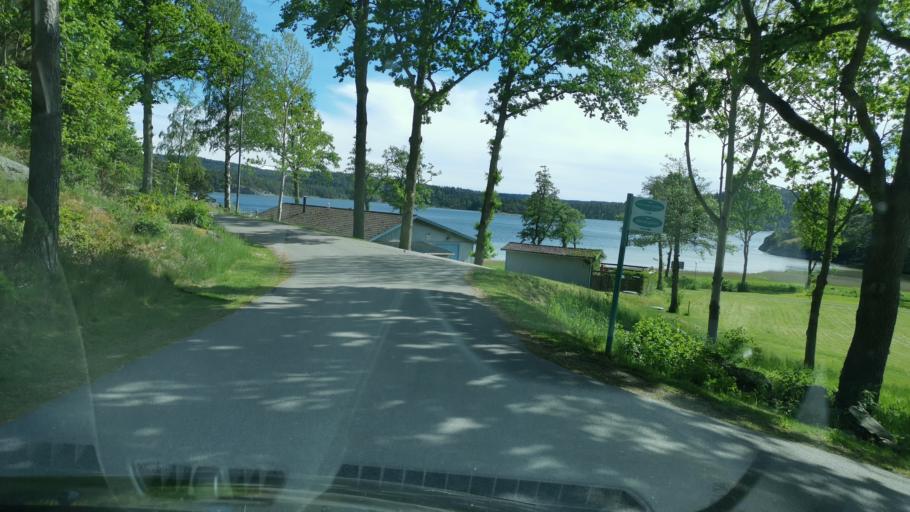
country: SE
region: Vaestra Goetaland
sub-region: Orust
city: Henan
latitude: 58.2619
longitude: 11.5967
